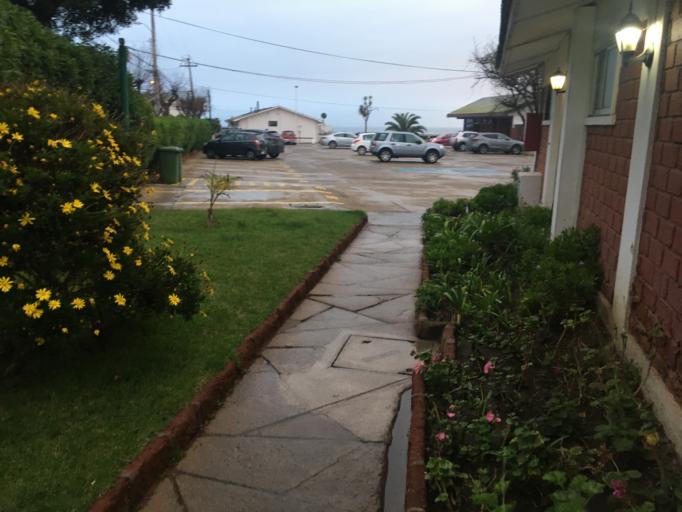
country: CL
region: Valparaiso
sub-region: Provincia de Valparaiso
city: Vina del Mar
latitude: -32.9194
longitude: -71.5187
